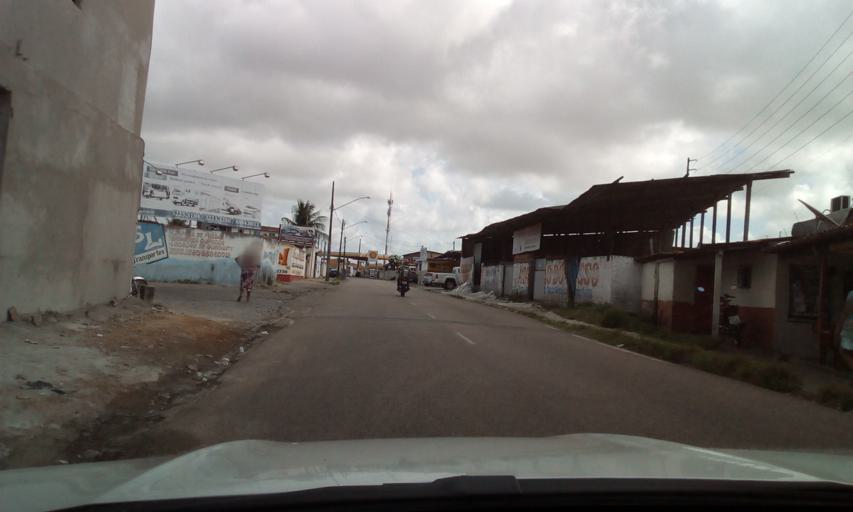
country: BR
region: Paraiba
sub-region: Joao Pessoa
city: Joao Pessoa
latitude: -7.1505
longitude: -34.8748
